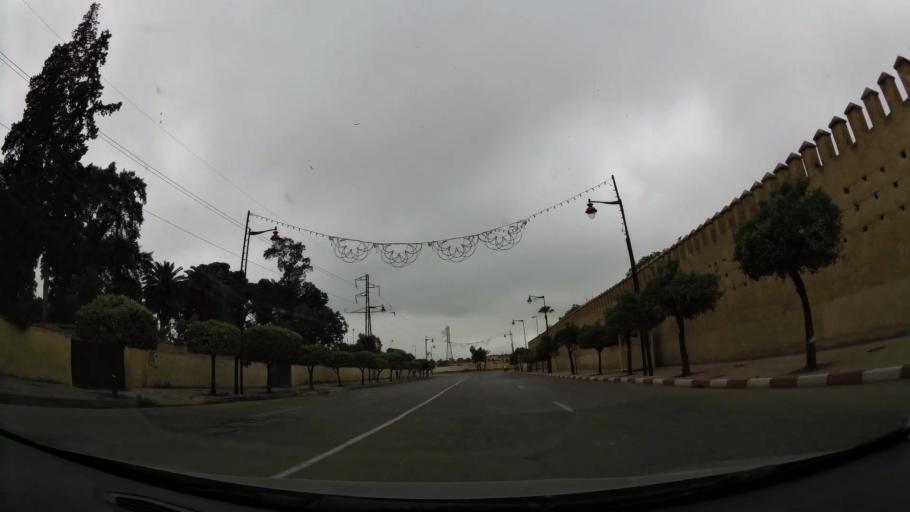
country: MA
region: Fes-Boulemane
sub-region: Fes
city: Fes
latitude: 34.0500
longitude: -5.0004
